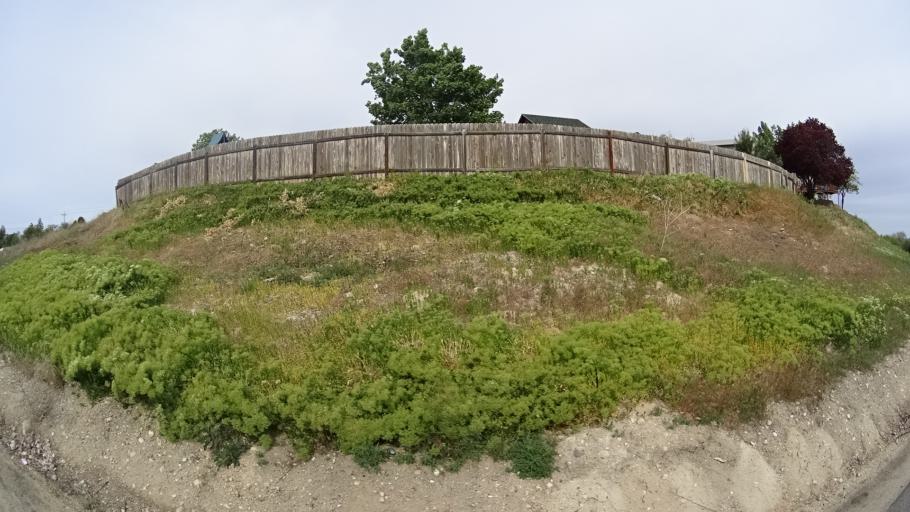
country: US
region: Idaho
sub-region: Ada County
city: Meridian
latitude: 43.5340
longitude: -116.3131
